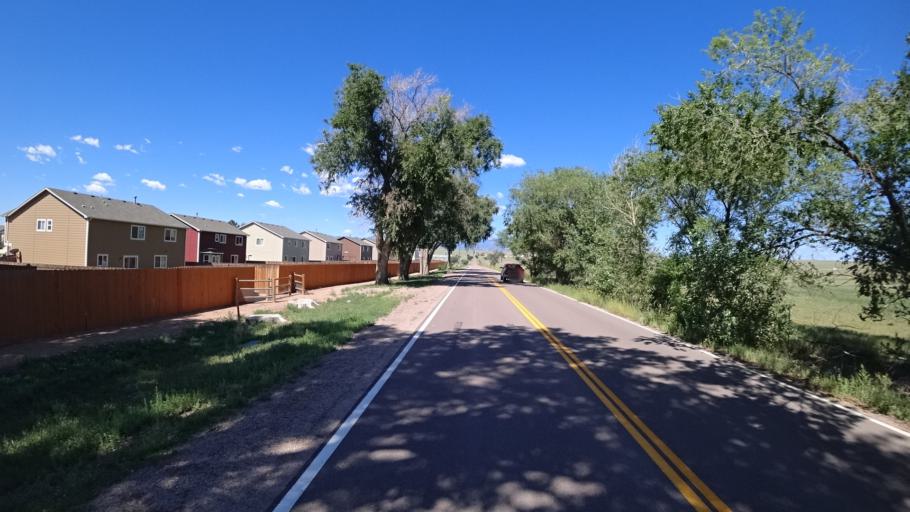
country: US
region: Colorado
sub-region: El Paso County
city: Security-Widefield
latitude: 38.7809
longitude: -104.6553
